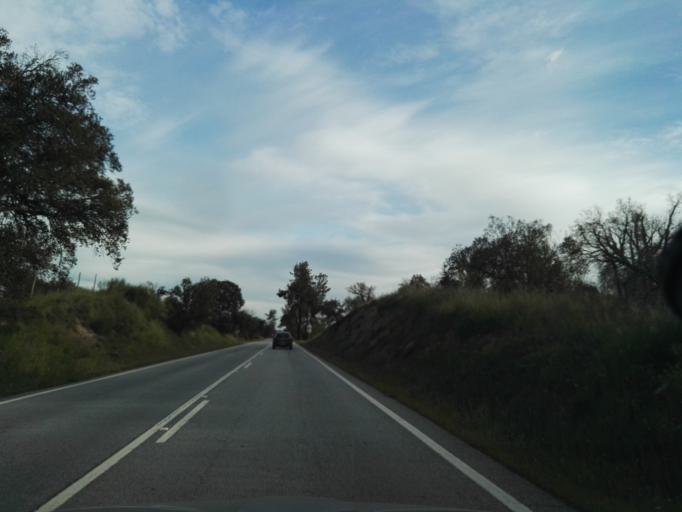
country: PT
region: Portalegre
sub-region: Arronches
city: Arronches
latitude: 39.0839
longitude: -7.2820
